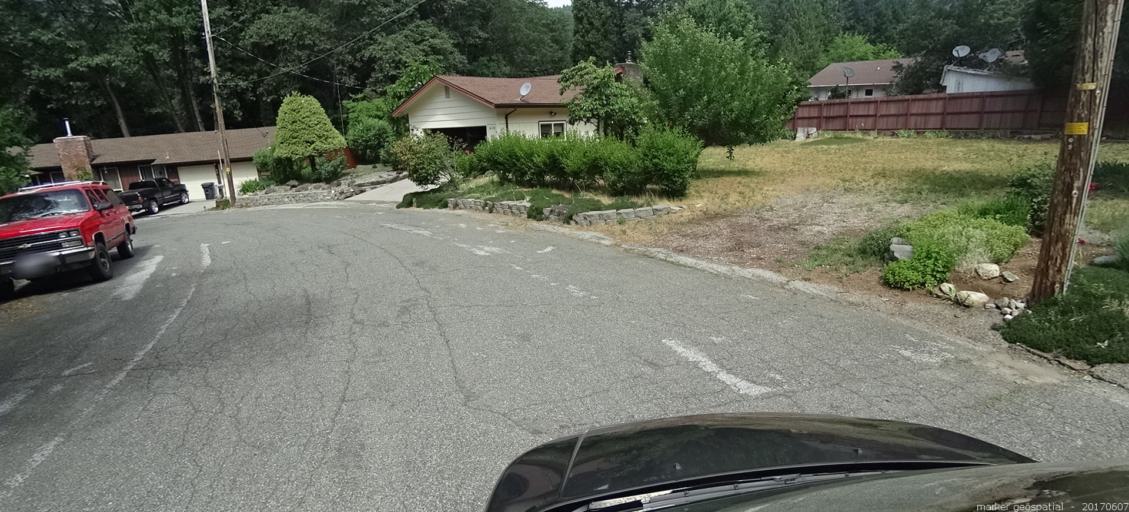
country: US
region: California
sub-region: Siskiyou County
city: Dunsmuir
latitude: 41.2352
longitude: -122.2737
